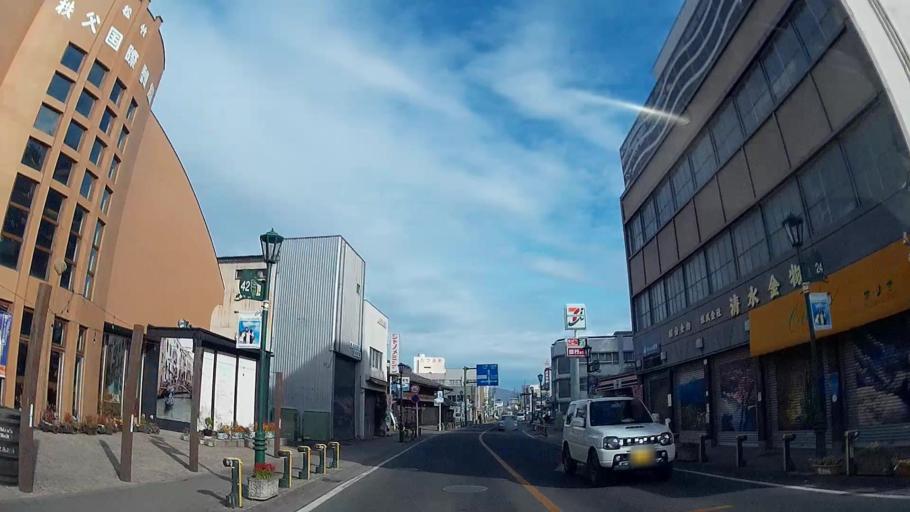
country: JP
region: Saitama
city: Chichibu
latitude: 35.9982
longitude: 139.0833
